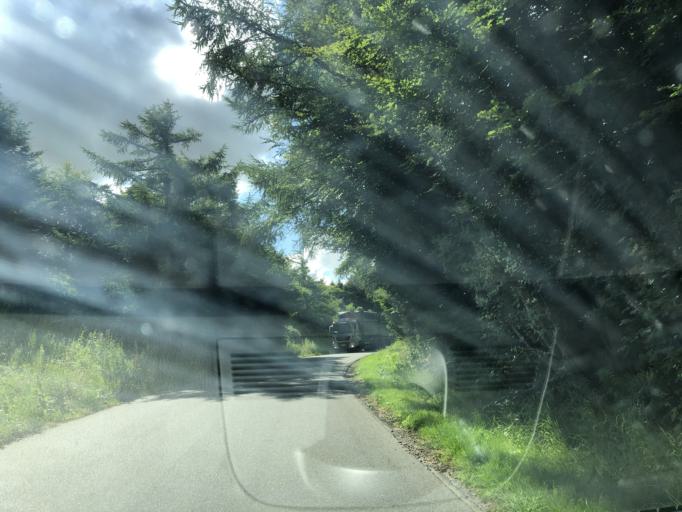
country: DK
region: Central Jutland
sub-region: Struer Kommune
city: Struer
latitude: 56.4785
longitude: 8.5220
